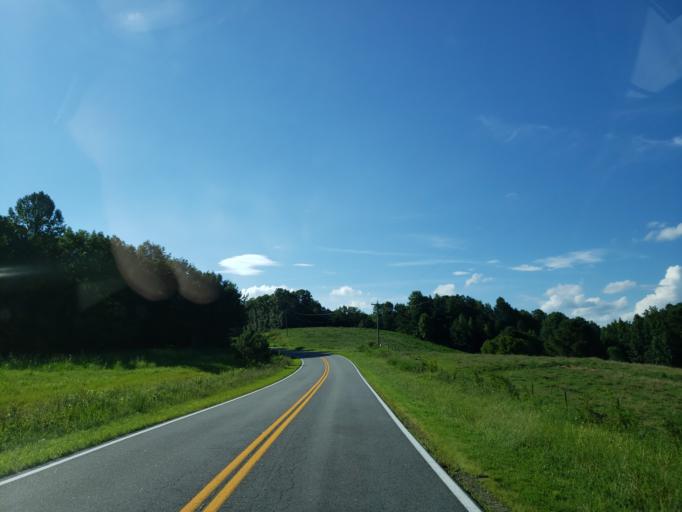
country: US
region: Georgia
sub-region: Bartow County
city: Rydal
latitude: 34.3507
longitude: -84.5987
